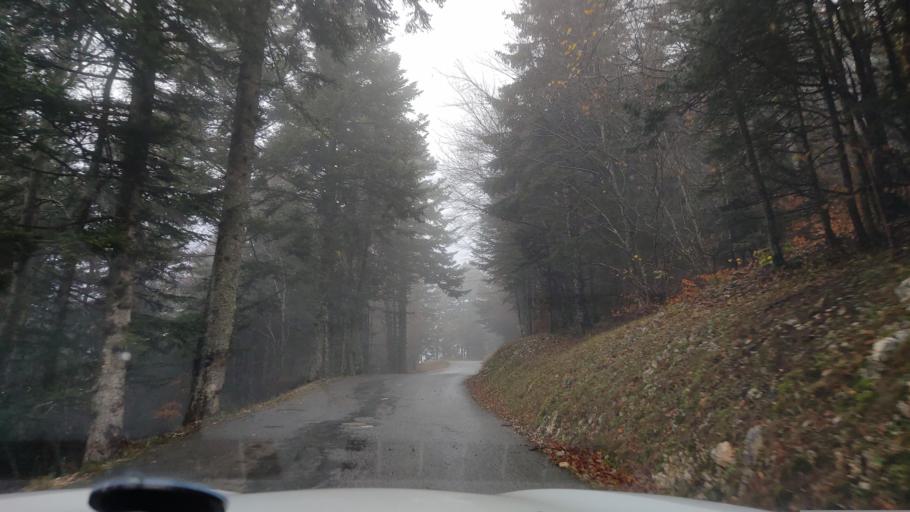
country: FR
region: Rhone-Alpes
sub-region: Departement de la Savoie
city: Le Bourget-du-Lac
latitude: 45.6568
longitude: 5.8136
